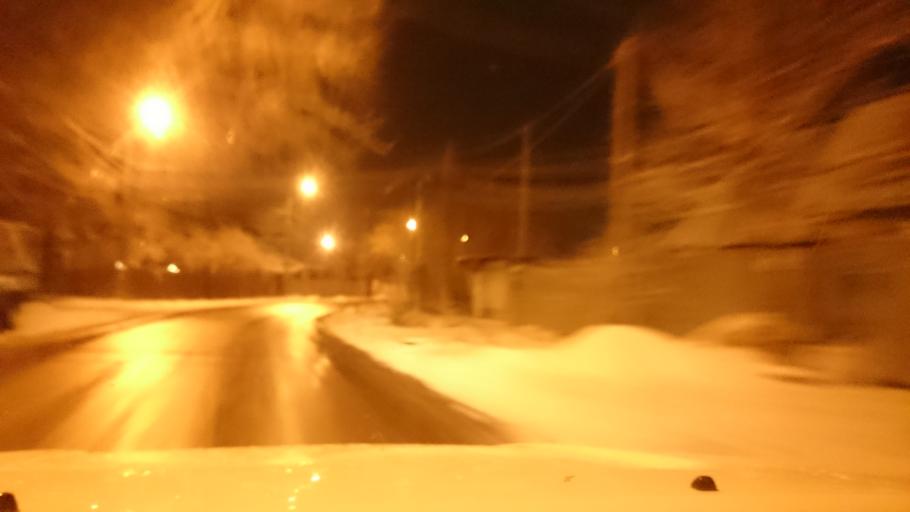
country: RU
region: Tula
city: Tula
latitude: 54.2056
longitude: 37.5527
